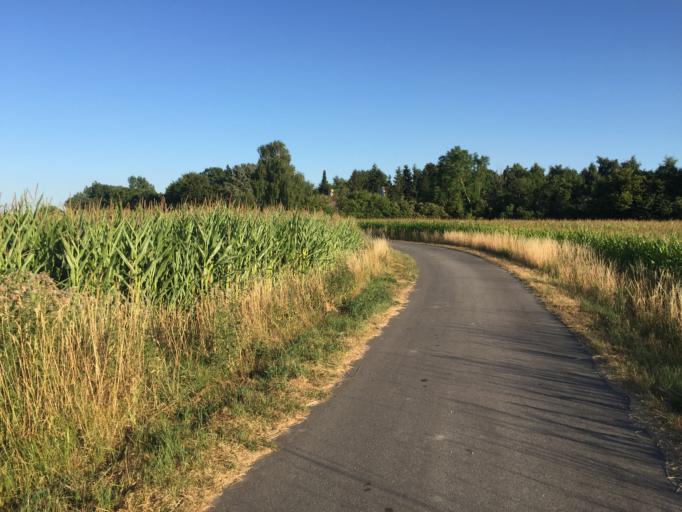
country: DK
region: South Denmark
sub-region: Odense Kommune
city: Bellinge
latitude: 55.3670
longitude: 10.2820
